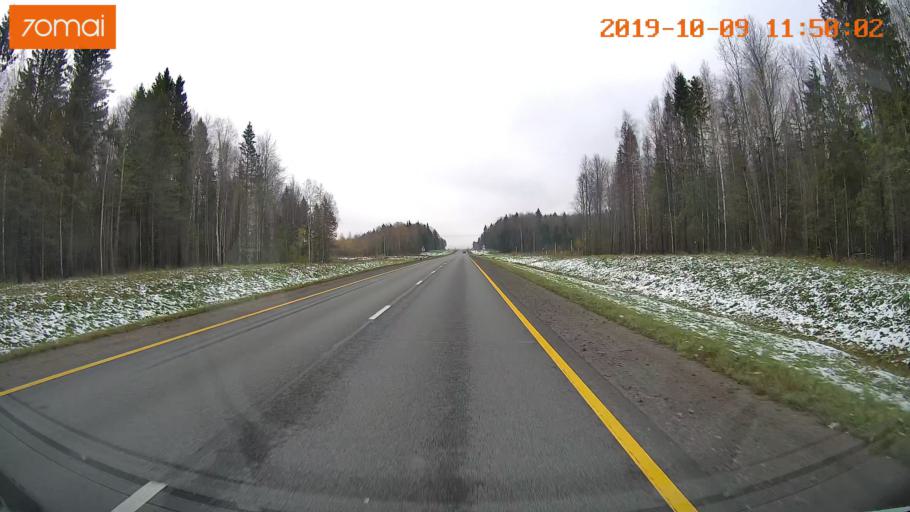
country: RU
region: Vologda
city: Gryazovets
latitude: 58.8106
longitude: 40.2400
